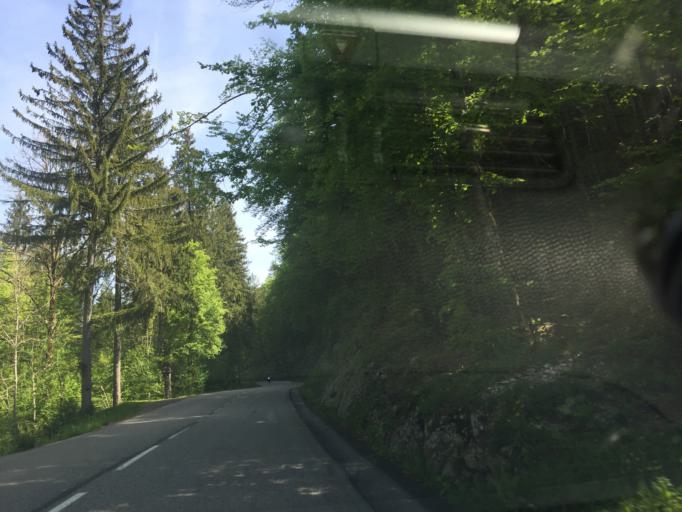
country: FR
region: Rhone-Alpes
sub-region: Departement de l'Isere
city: Saint-Vincent-de-Mercuze
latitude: 45.4381
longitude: 5.8774
